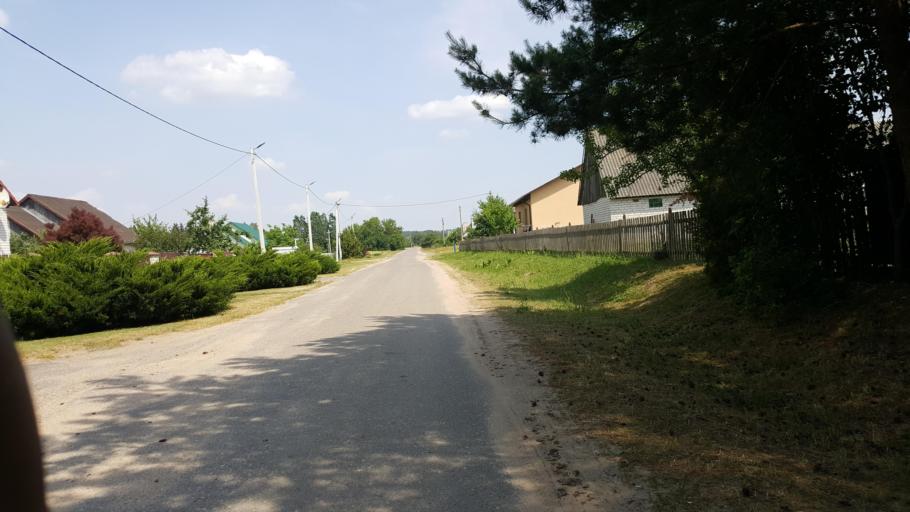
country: BY
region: Brest
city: Kamyanyets
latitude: 52.3318
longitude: 23.7779
